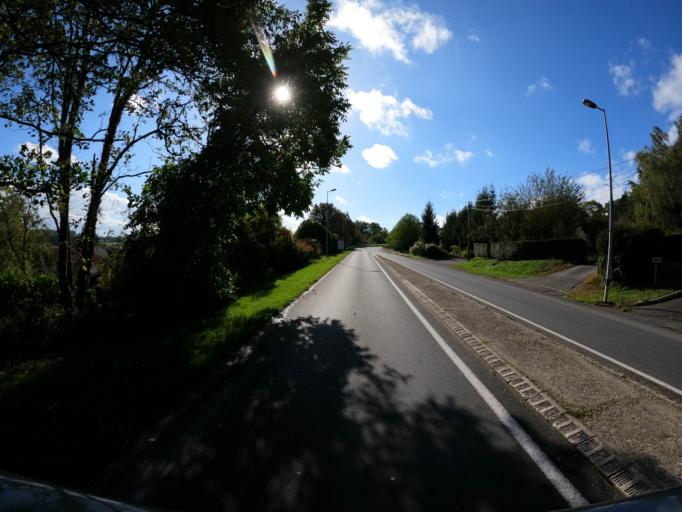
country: FR
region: Ile-de-France
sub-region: Departement de Seine-et-Marne
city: Montry
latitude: 48.8824
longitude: 2.8267
